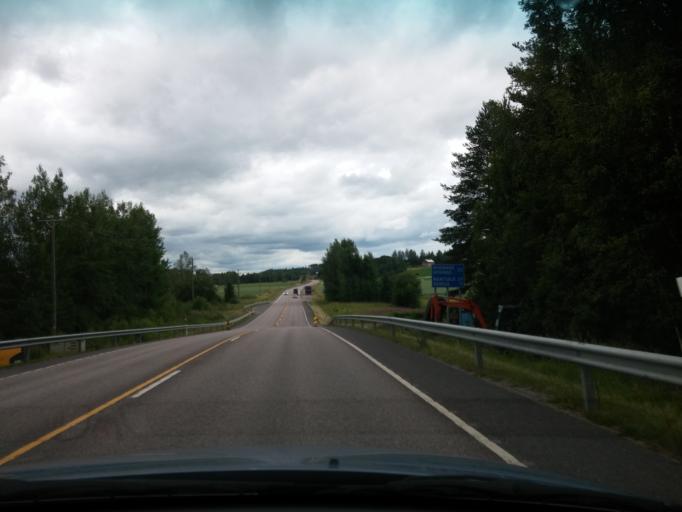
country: FI
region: Uusimaa
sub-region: Porvoo
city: Askola
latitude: 60.4517
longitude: 25.5840
